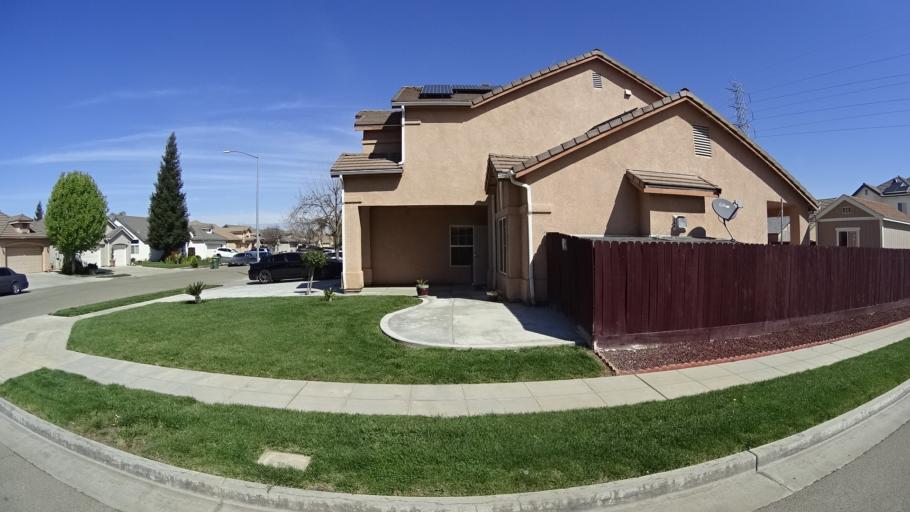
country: US
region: California
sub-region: Fresno County
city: Biola
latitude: 36.8159
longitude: -119.9015
